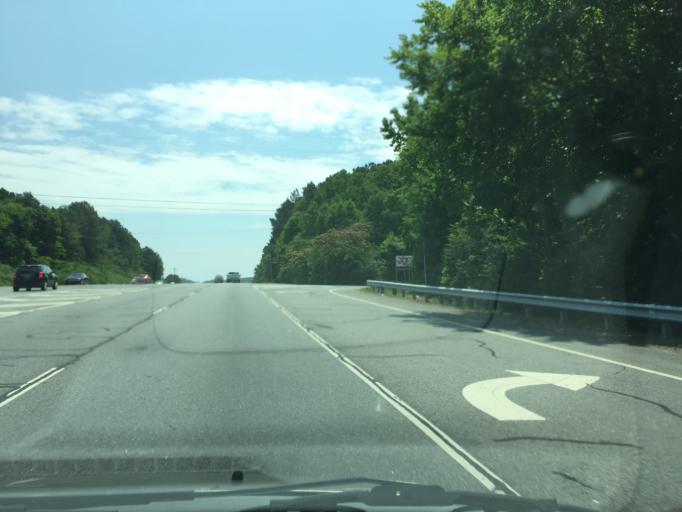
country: US
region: Georgia
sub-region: Catoosa County
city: Indian Springs
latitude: 34.9357
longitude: -85.1992
